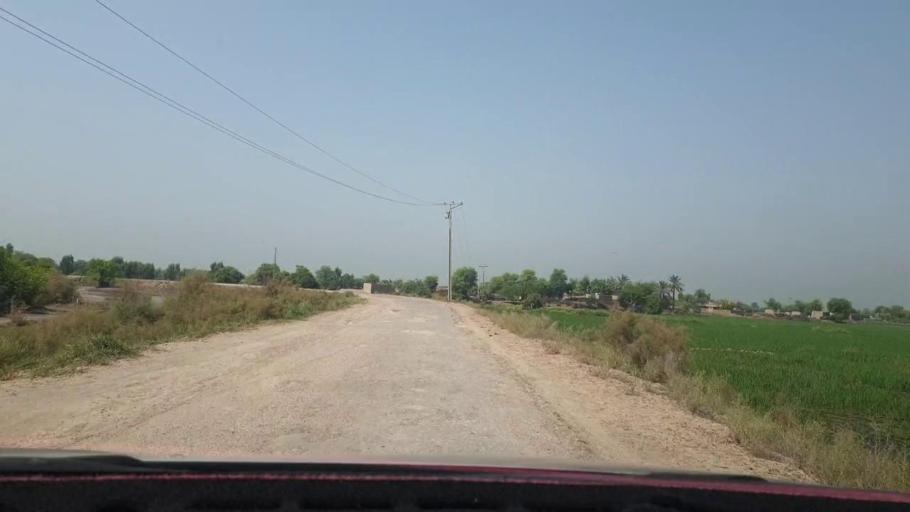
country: PK
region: Sindh
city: Warah
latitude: 27.4177
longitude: 67.8456
